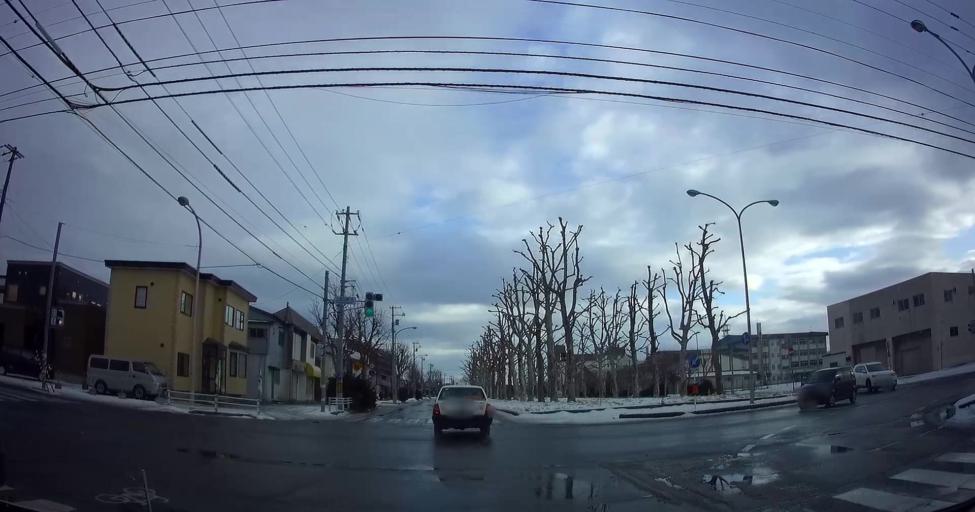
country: JP
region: Hokkaido
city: Hakodate
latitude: 41.7796
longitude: 140.7357
